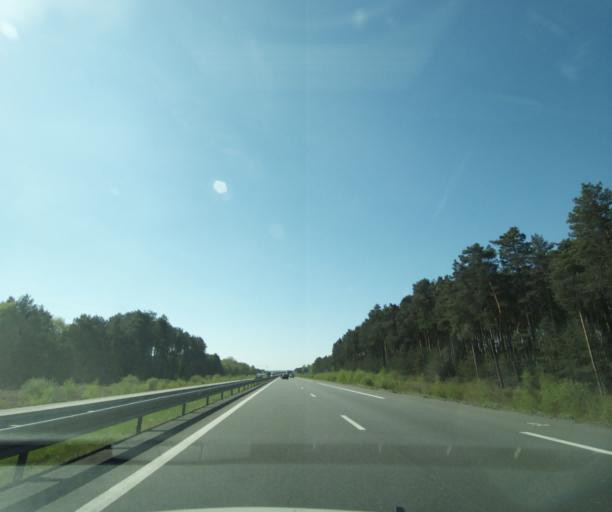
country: FR
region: Centre
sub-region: Departement du Loir-et-Cher
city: Theillay
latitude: 47.3575
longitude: 2.0515
